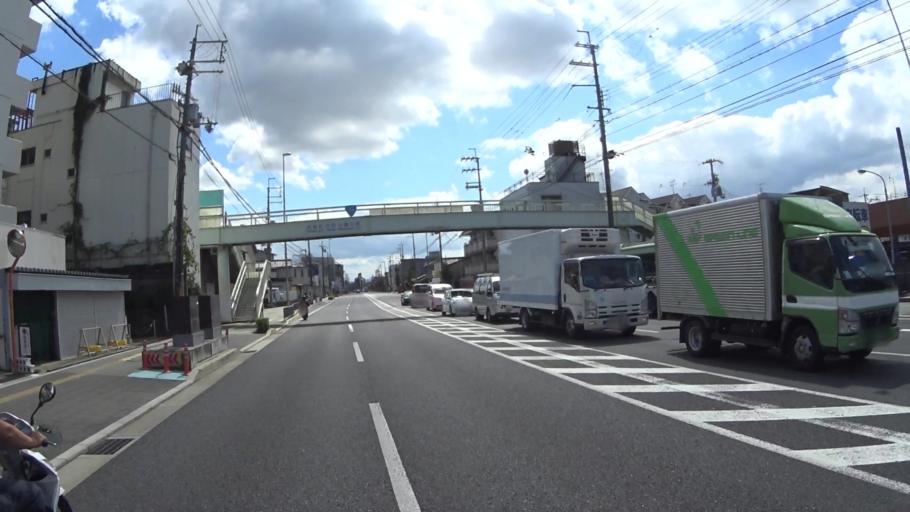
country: JP
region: Kyoto
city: Muko
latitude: 34.9547
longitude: 135.7600
